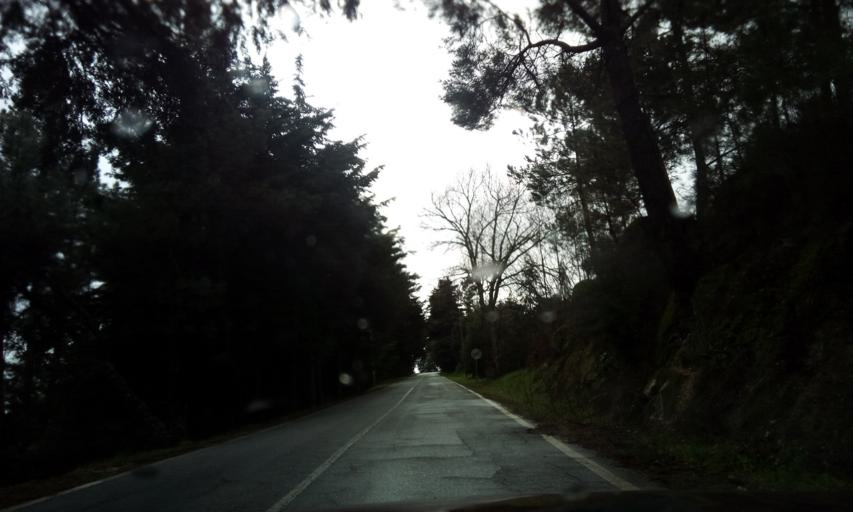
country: PT
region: Guarda
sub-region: Fornos de Algodres
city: Fornos de Algodres
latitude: 40.6091
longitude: -7.5794
